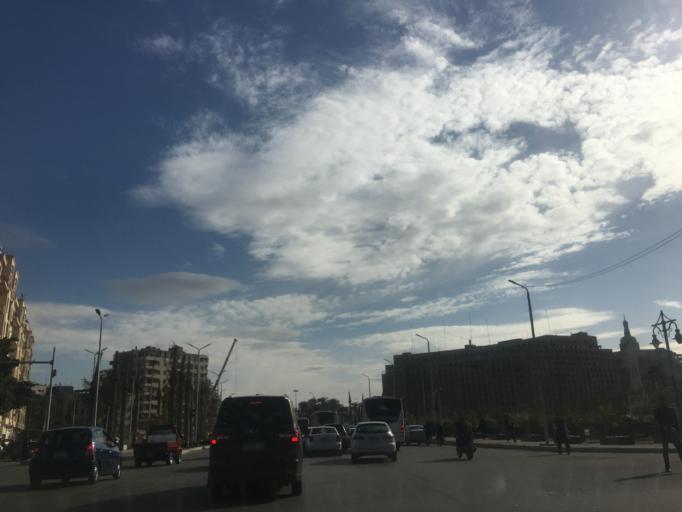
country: EG
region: Muhafazat al Qahirah
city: Cairo
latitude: 30.0463
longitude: 31.2347
